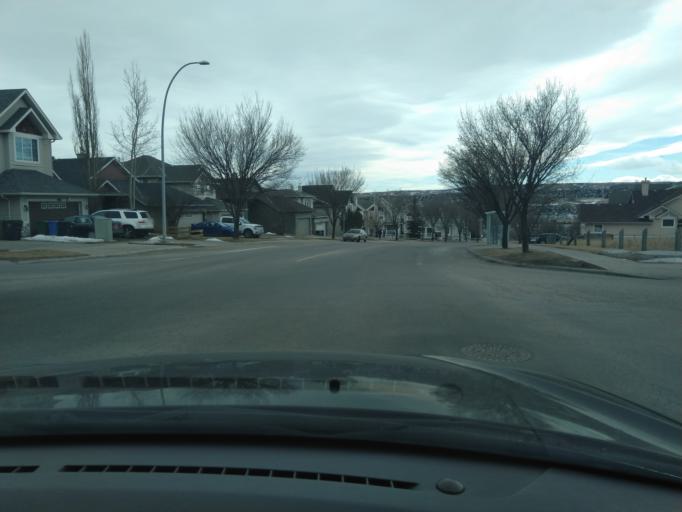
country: CA
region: Alberta
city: Calgary
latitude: 51.1600
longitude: -114.1009
